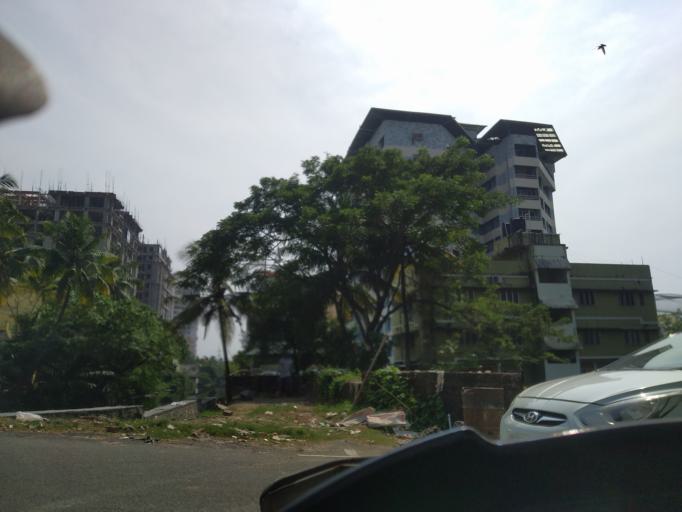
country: IN
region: Kerala
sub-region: Ernakulam
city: Cochin
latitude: 9.9550
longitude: 76.2990
